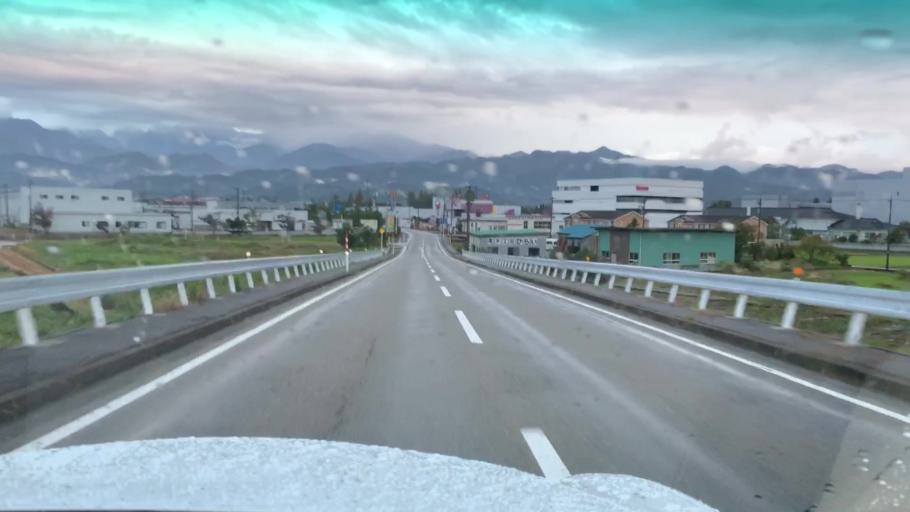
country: JP
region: Toyama
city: Kamiichi
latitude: 36.7020
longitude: 137.3375
